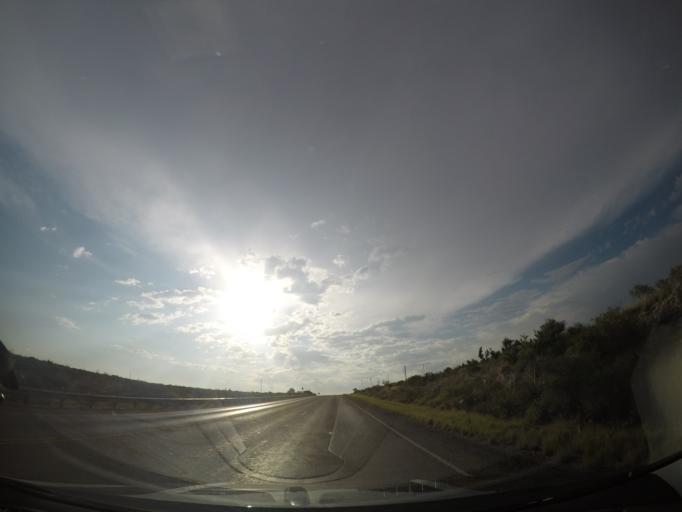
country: US
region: Texas
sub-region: Terrell County
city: Sanderson
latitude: 30.0589
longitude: -102.2539
